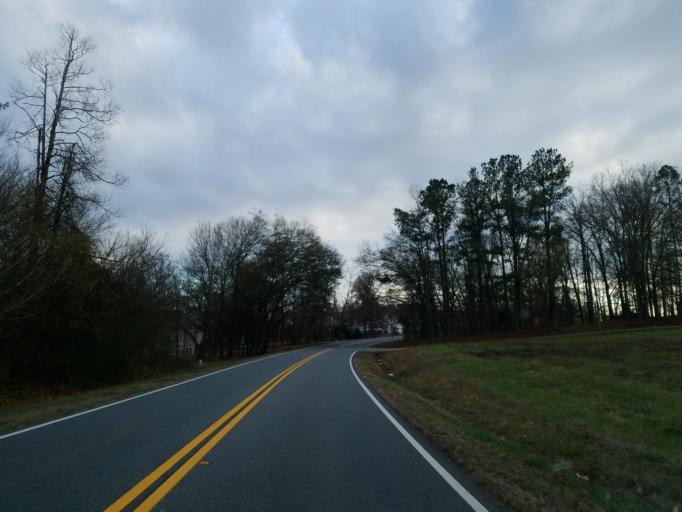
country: US
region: Georgia
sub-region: Forsyth County
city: Cumming
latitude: 34.2888
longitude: -84.0879
